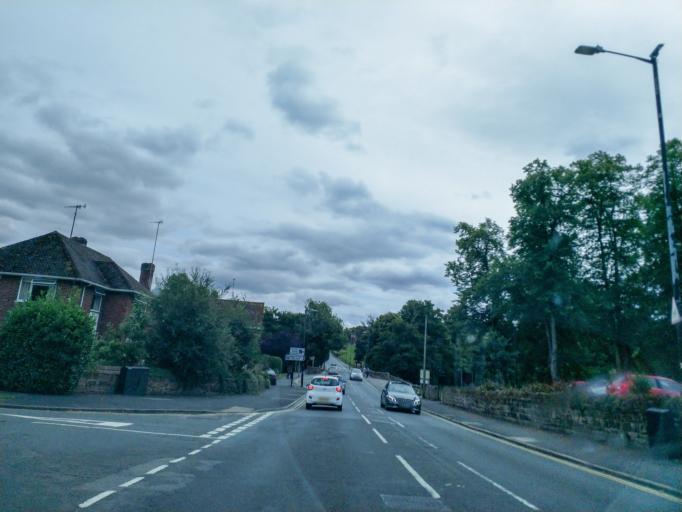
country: GB
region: England
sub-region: Warwickshire
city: Kenilworth
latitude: 52.3494
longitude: -1.5804
